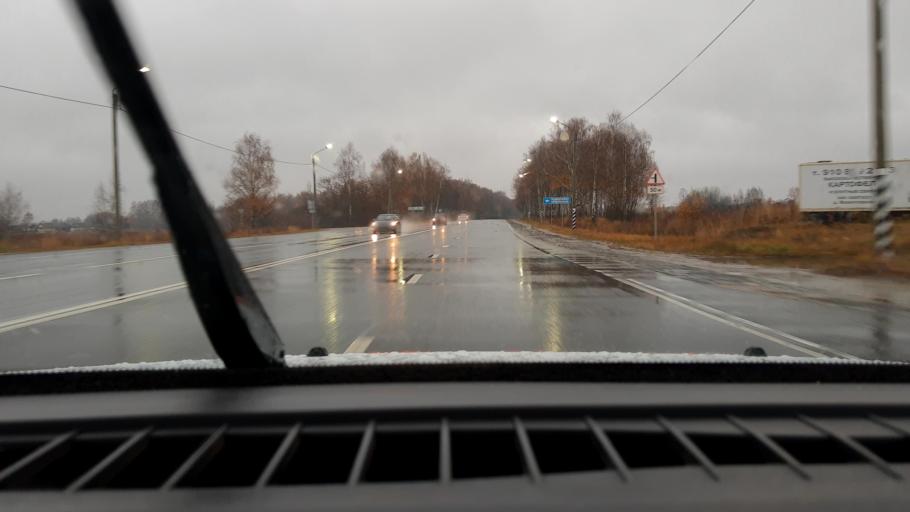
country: RU
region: Nizjnij Novgorod
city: Sitniki
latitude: 56.5070
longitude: 44.0234
